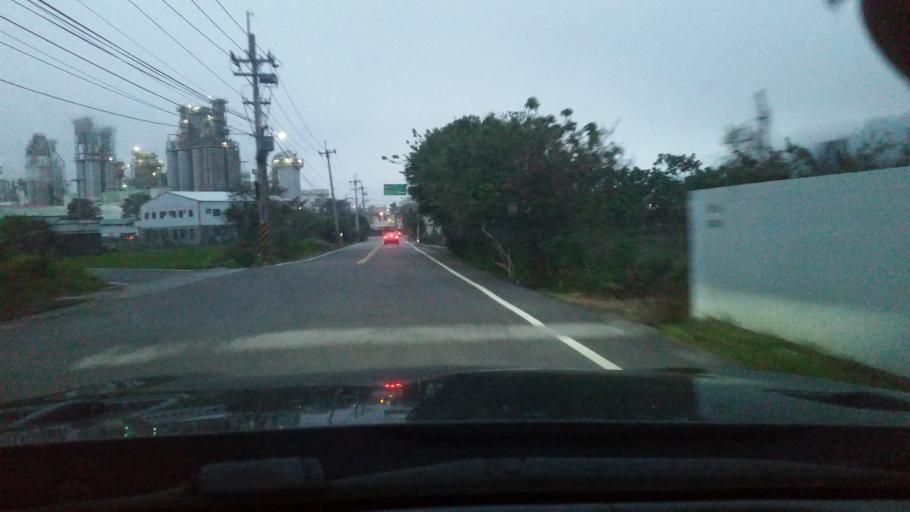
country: TW
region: Taiwan
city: Fengyuan
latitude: 24.3518
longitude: 120.7424
